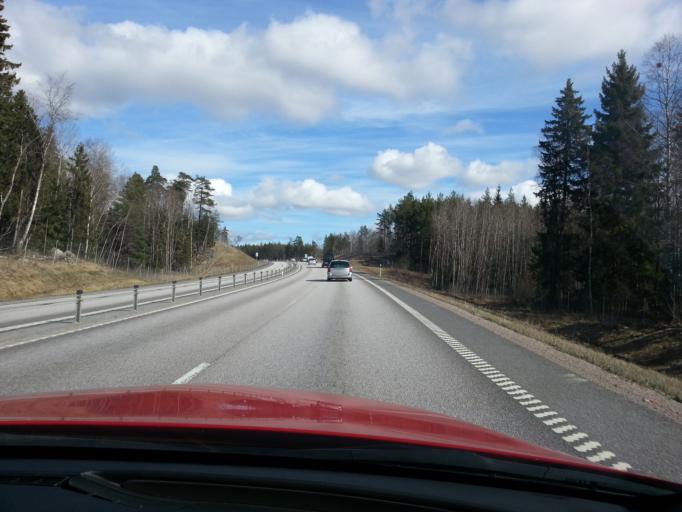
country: SE
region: Uppsala
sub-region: Uppsala Kommun
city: Storvreta
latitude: 59.9271
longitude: 17.7911
